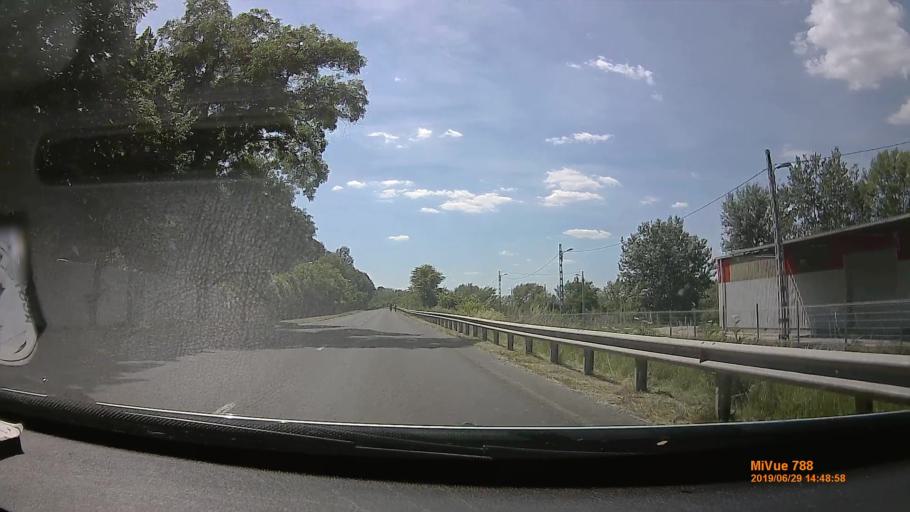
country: HU
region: Komarom-Esztergom
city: Labatlan
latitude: 47.7509
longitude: 18.5017
